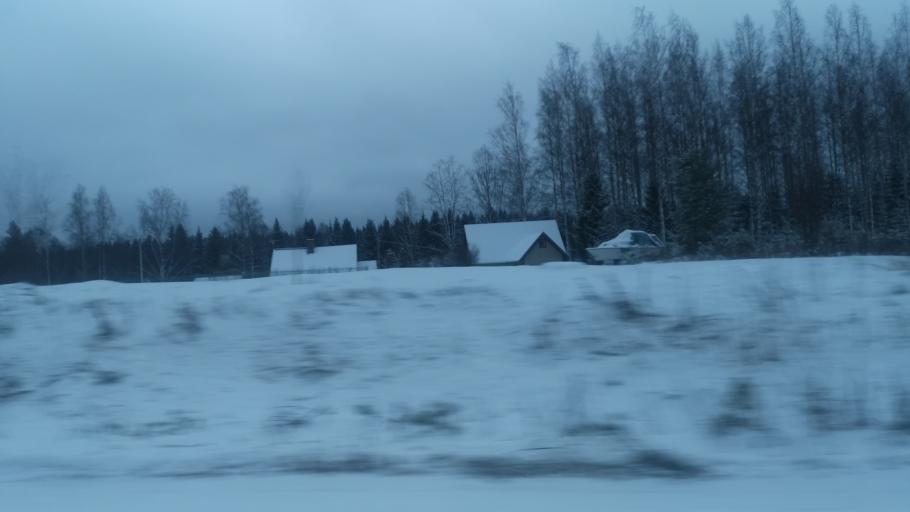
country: FI
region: Southern Savonia
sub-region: Savonlinna
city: Savonlinna
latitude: 61.9921
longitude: 28.7717
